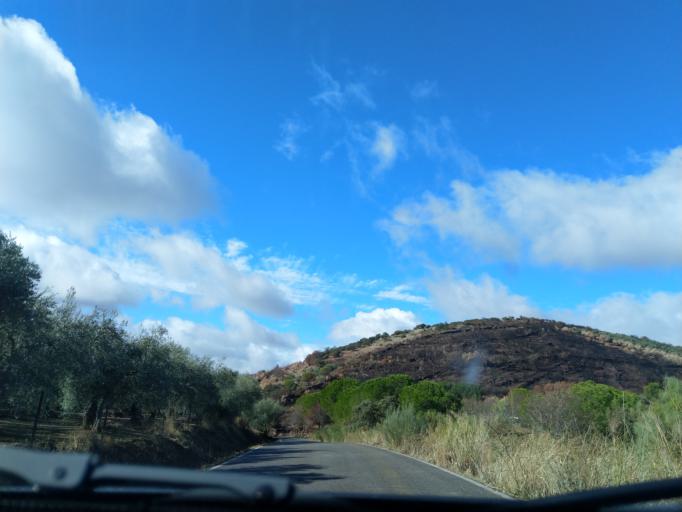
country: ES
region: Extremadura
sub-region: Provincia de Badajoz
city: Reina
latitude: 38.1478
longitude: -5.9113
